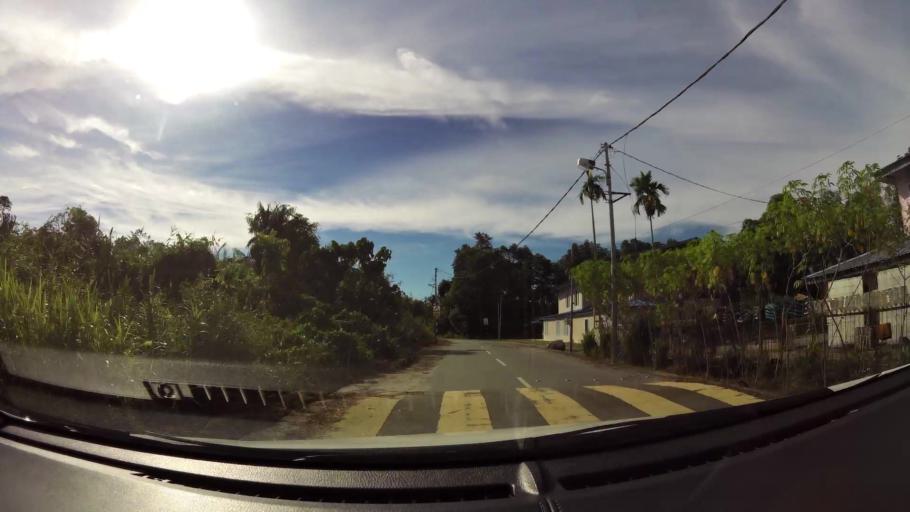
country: BN
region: Brunei and Muara
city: Bandar Seri Begawan
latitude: 4.9798
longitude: 115.0229
